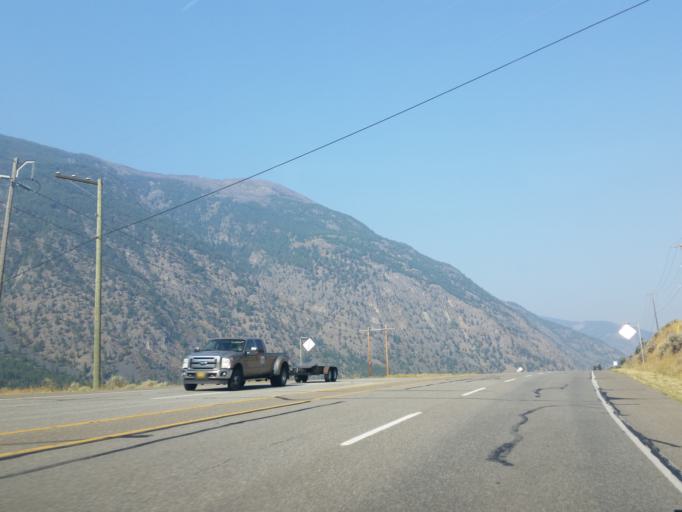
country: CA
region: British Columbia
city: Oliver
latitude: 49.2047
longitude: -119.8657
